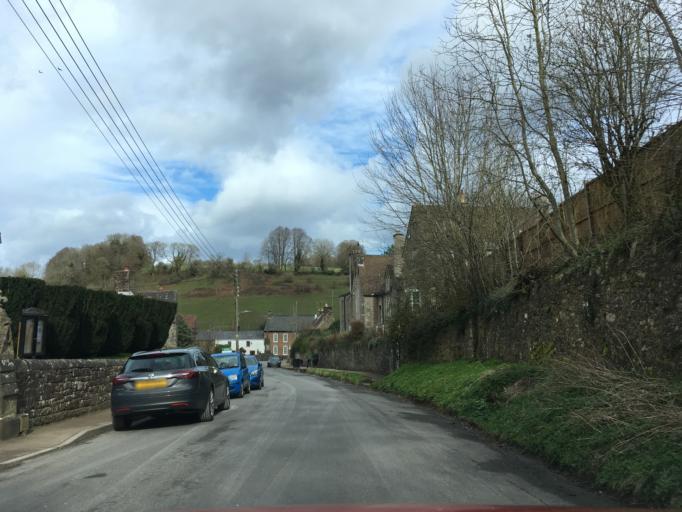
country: GB
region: England
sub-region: Gloucestershire
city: Coleford
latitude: 51.7686
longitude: -2.6225
